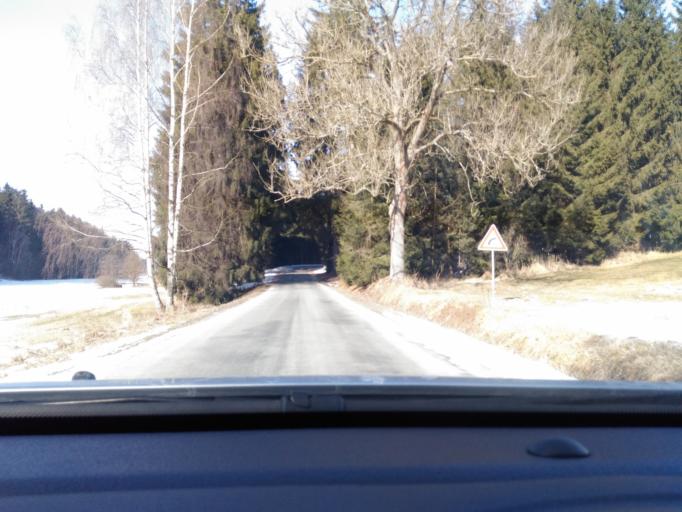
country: CZ
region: Vysocina
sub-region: Okres Zd'ar nad Sazavou
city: Nove Mesto na Morave
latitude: 49.5405
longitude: 16.0520
